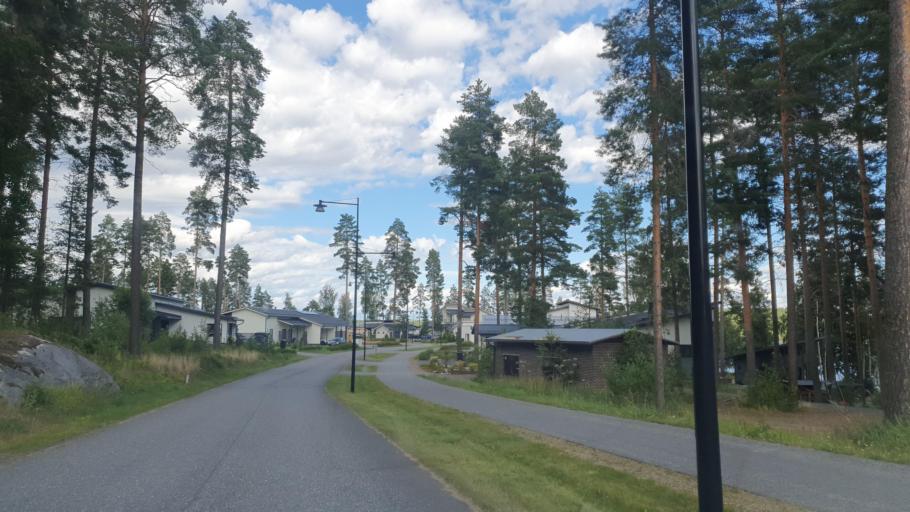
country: FI
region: Central Finland
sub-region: Jyvaeskylae
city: Saeynaetsalo
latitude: 62.1608
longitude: 25.7667
